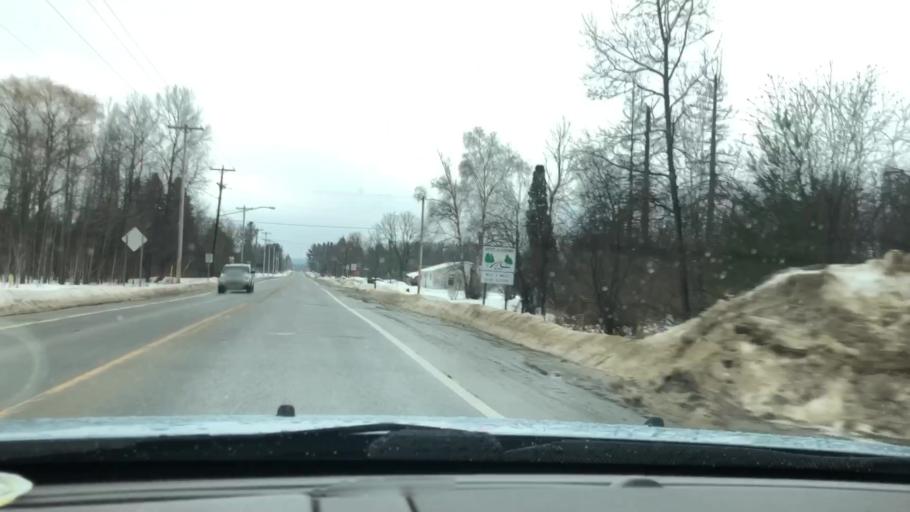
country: US
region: Michigan
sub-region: Charlevoix County
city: East Jordan
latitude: 45.1512
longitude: -85.1192
